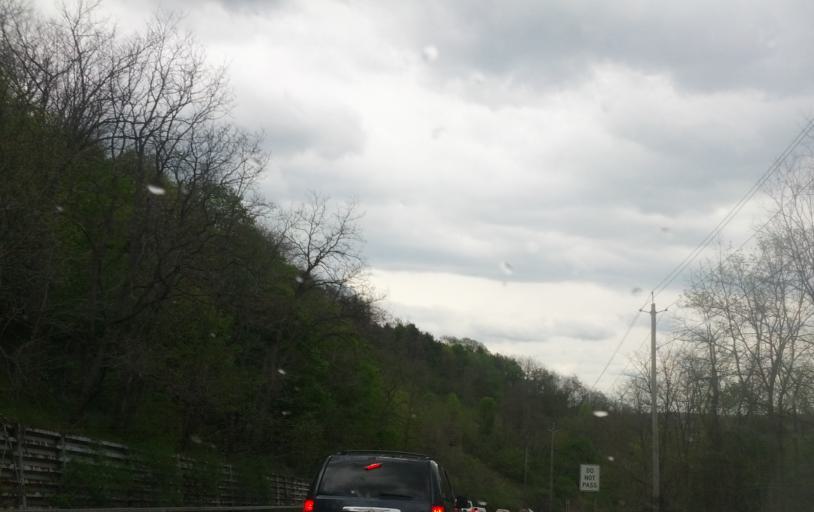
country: US
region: New York
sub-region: Onondaga County
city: Nedrow
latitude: 43.0055
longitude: -76.1662
